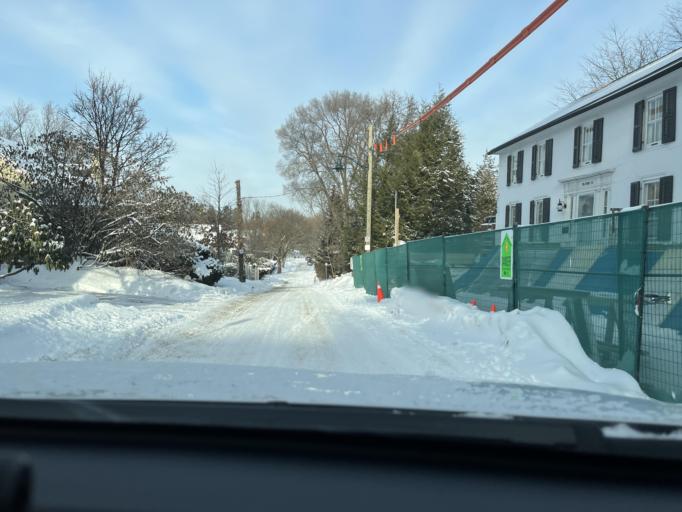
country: CA
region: Ontario
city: Oakville
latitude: 43.4432
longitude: -79.6658
